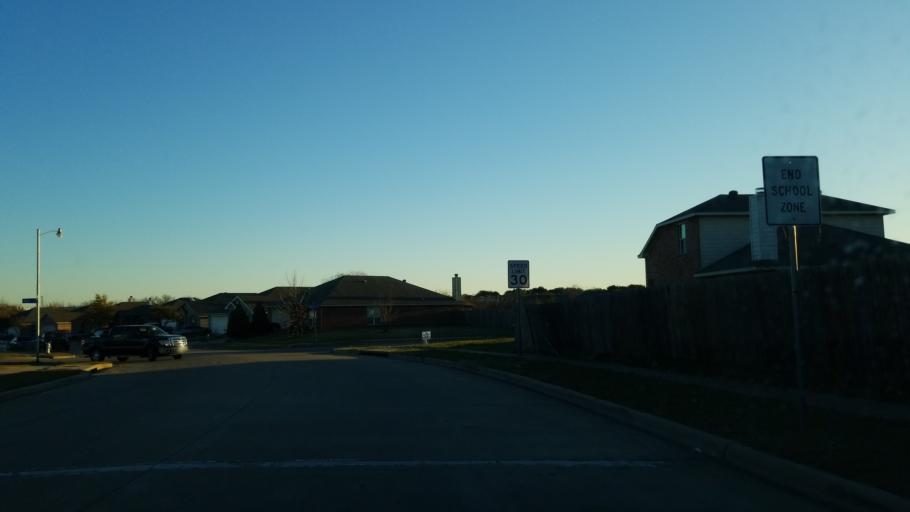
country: US
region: Texas
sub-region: Tarrant County
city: Arlington
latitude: 32.7278
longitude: -97.0540
